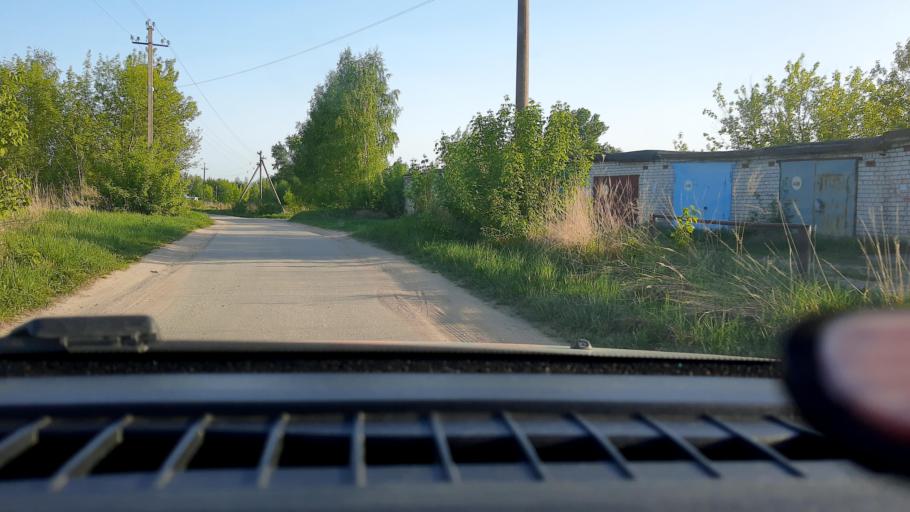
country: RU
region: Nizjnij Novgorod
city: Kstovo
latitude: 56.1339
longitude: 44.1913
